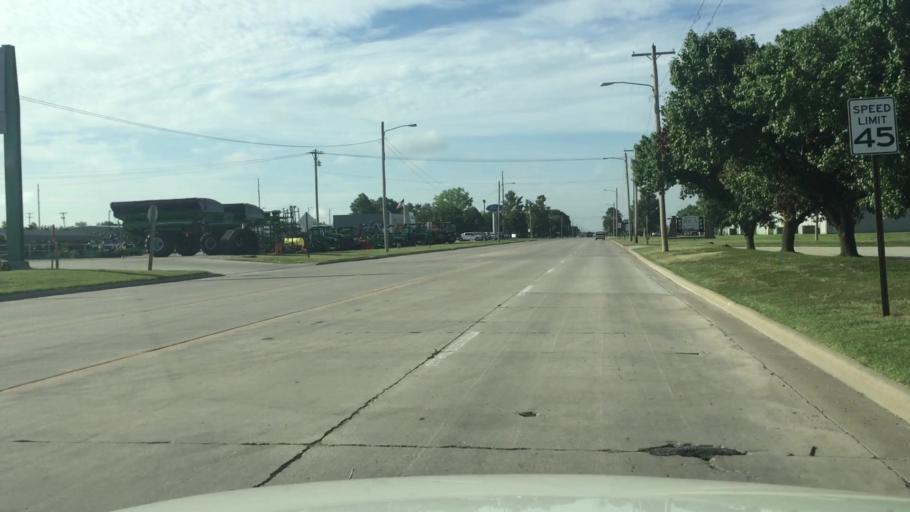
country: US
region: Kansas
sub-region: Allen County
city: Iola
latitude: 37.9466
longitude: -95.4091
